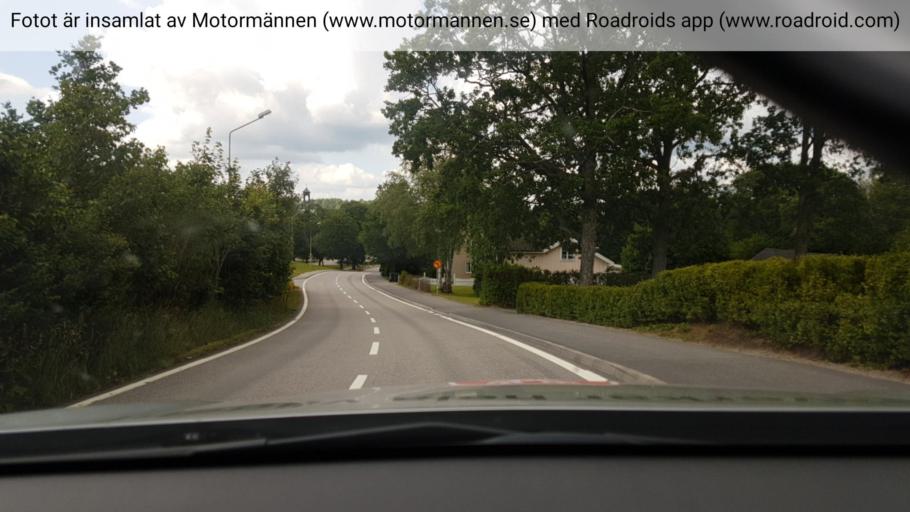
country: SE
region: Vaestra Goetaland
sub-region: Svenljunga Kommun
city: Svenljunga
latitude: 57.4950
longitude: 13.1212
